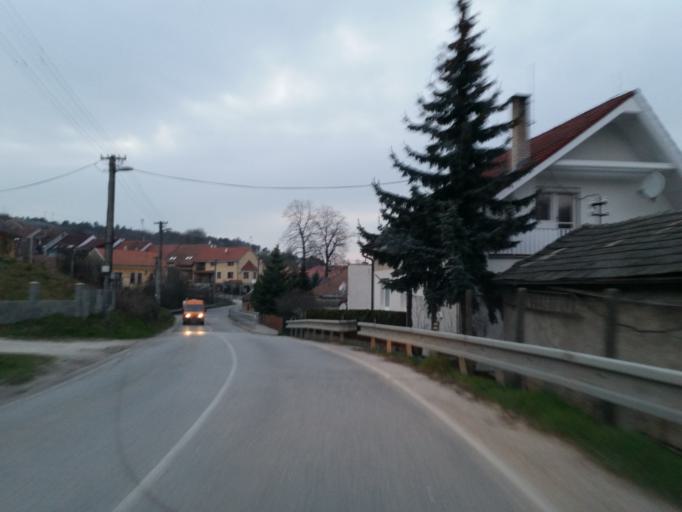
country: SK
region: Trnavsky
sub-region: Okres Trnava
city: Piestany
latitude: 48.5814
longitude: 17.8521
